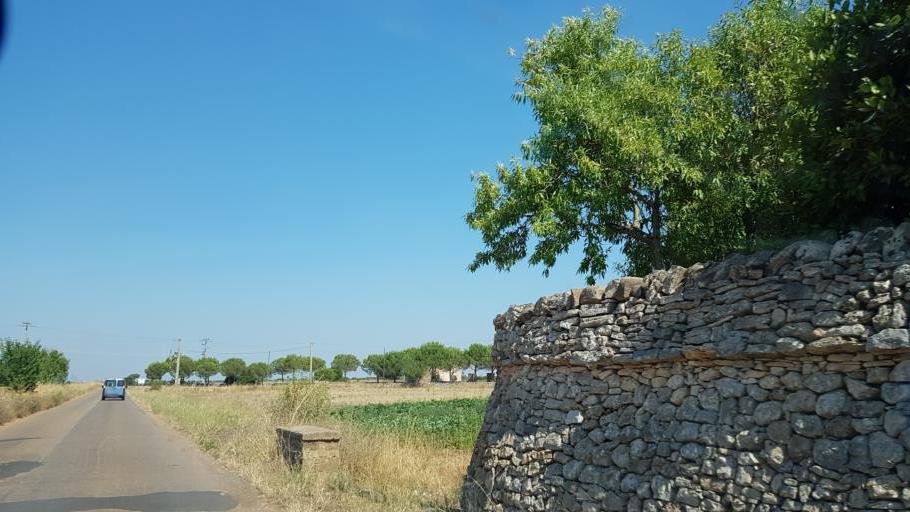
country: IT
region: Apulia
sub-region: Provincia di Lecce
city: Nardo
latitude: 40.1741
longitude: 17.9662
